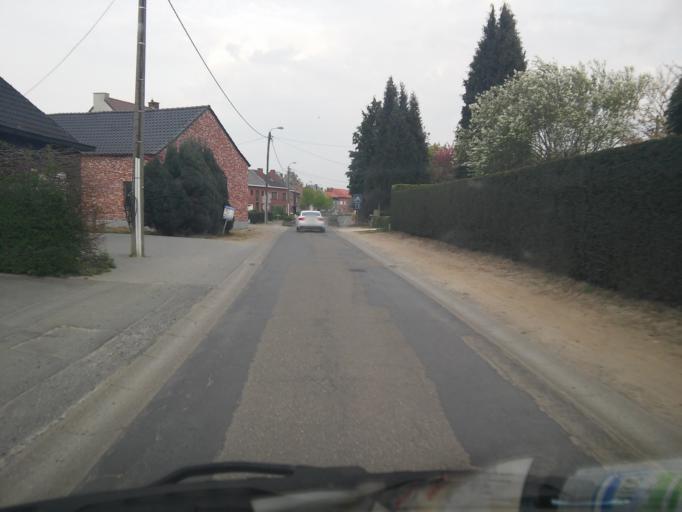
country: BE
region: Flanders
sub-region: Provincie Antwerpen
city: Mechelen
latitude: 51.0246
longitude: 4.4564
